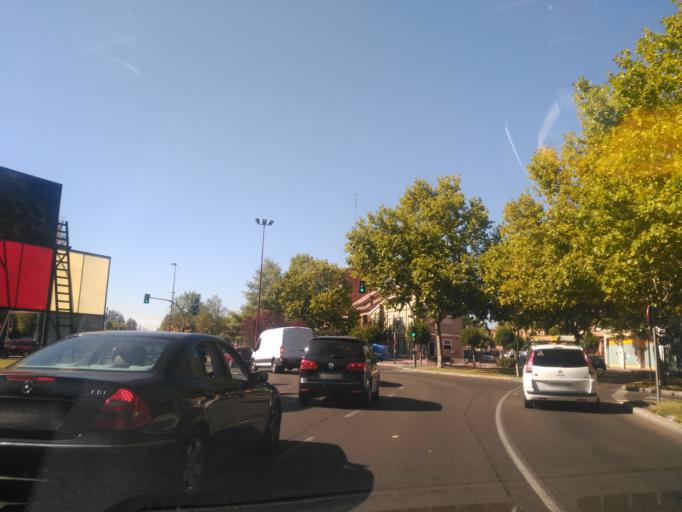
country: ES
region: Castille and Leon
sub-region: Provincia de Valladolid
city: Valladolid
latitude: 41.6284
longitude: -4.7434
